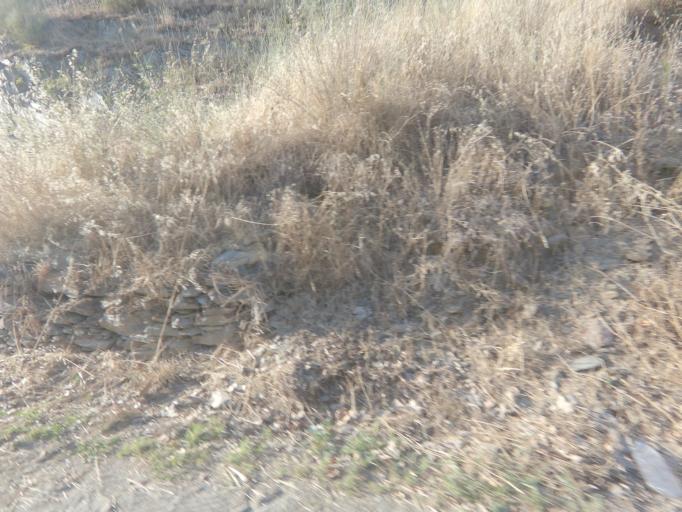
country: PT
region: Viseu
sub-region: Tabuaco
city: Tabuaco
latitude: 41.1619
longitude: -7.6107
